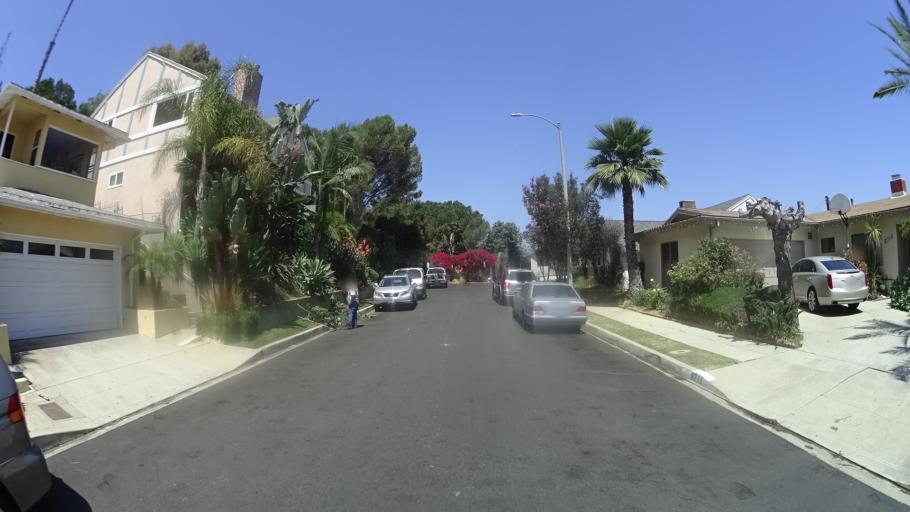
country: US
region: California
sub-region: Los Angeles County
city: Ladera Heights
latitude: 34.0166
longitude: -118.3707
